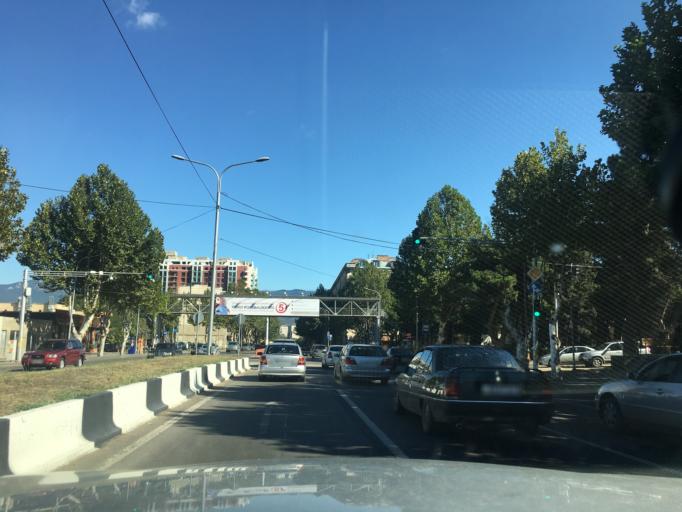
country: GE
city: Zahesi
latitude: 41.7692
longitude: 44.7923
